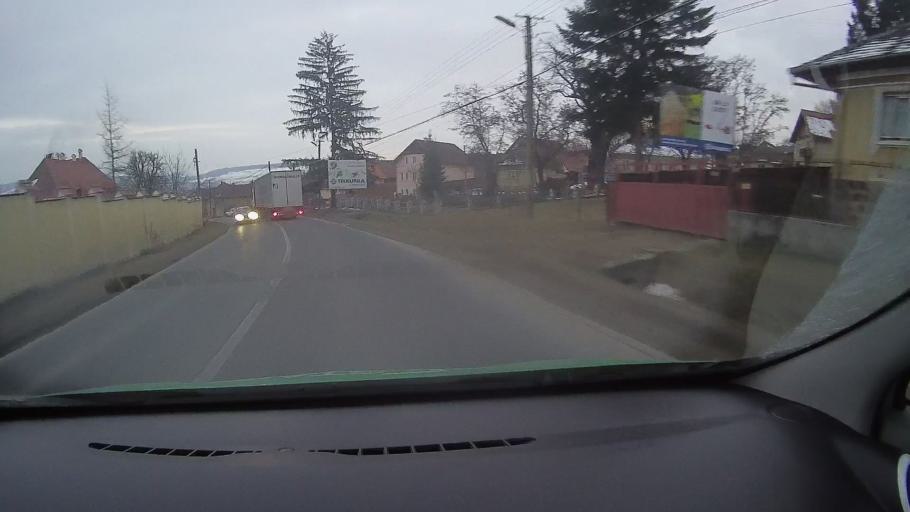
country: RO
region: Harghita
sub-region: Municipiul Odorheiu Secuiesc
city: Odorheiu Secuiesc
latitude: 46.3168
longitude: 25.2810
